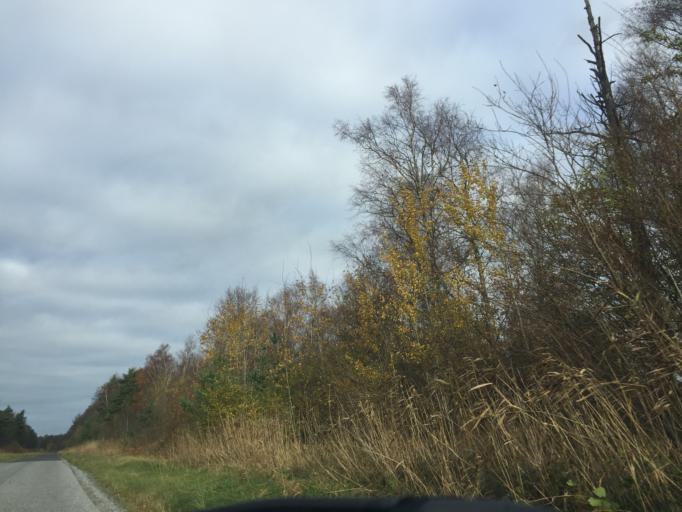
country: LV
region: Liepaja
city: Vec-Liepaja
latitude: 56.5652
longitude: 21.0552
